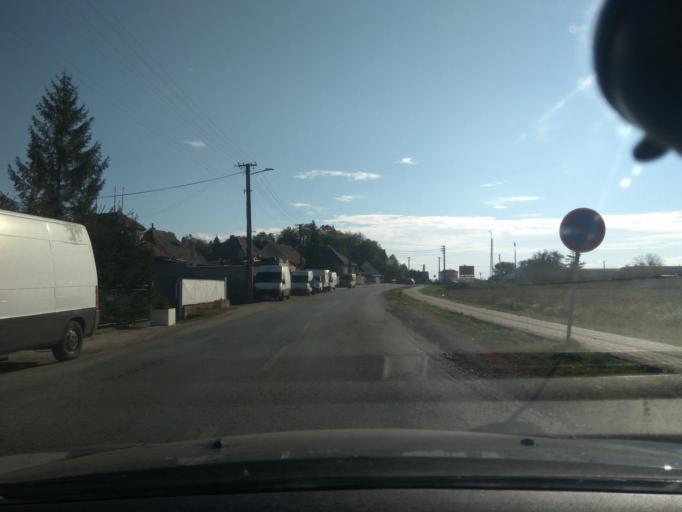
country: SK
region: Trnavsky
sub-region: Okres Trnava
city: Piestany
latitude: 48.5631
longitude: 17.8390
